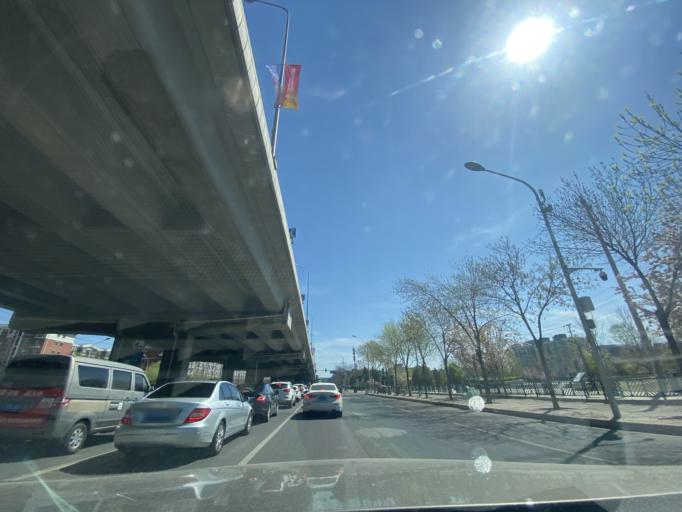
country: CN
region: Beijing
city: Sijiqing
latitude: 39.9229
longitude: 116.2530
